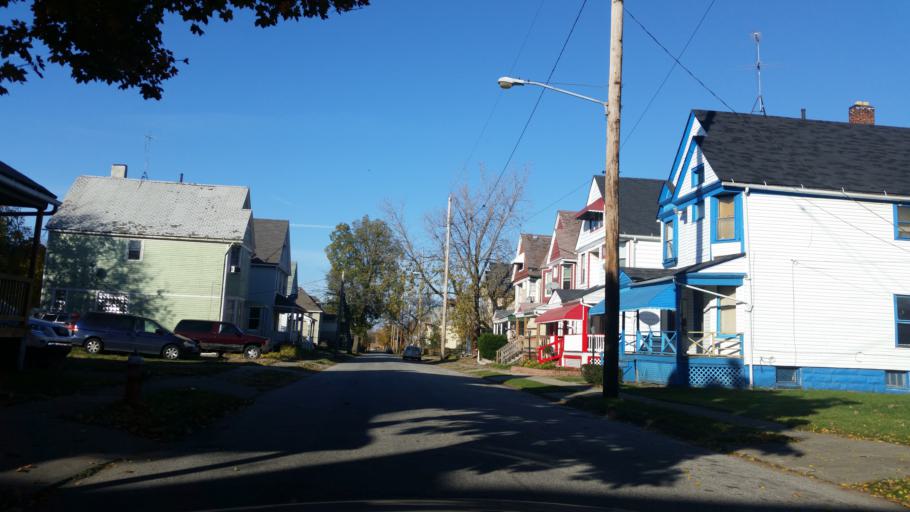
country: US
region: Ohio
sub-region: Cuyahoga County
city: Bratenahl
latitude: 41.4969
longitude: -81.6285
